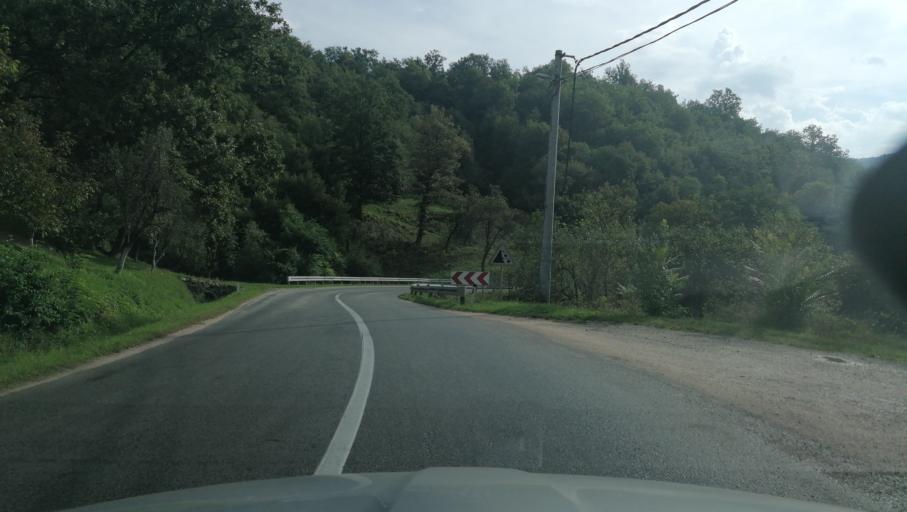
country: BA
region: Republika Srpska
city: Hiseti
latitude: 44.6754
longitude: 17.1486
